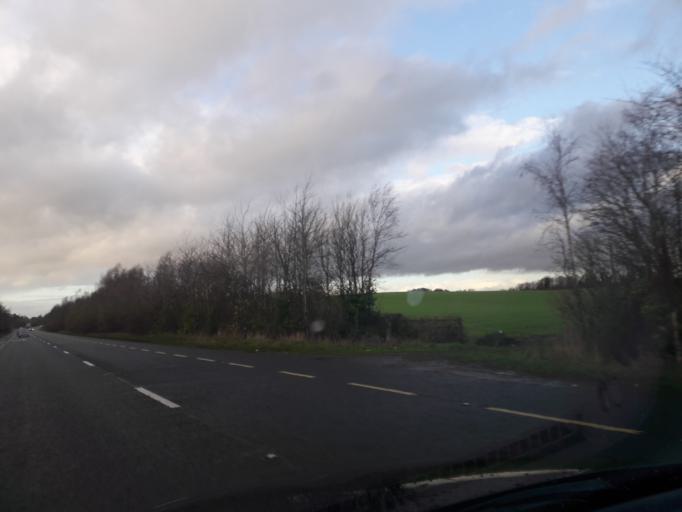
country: IE
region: Leinster
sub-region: Lu
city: Ardee
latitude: 53.8743
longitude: -6.5561
